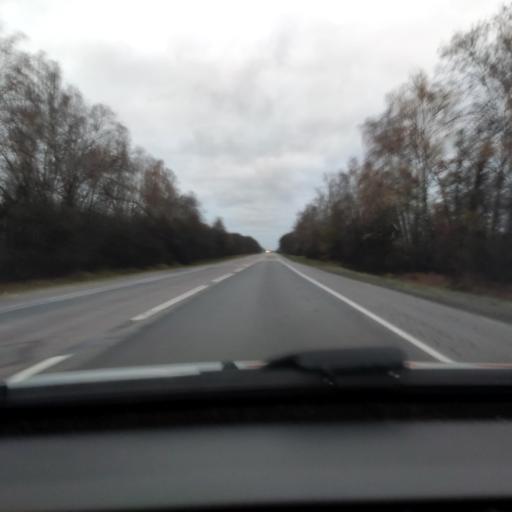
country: RU
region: Lipetsk
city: Khlevnoye
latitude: 52.3011
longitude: 39.1670
